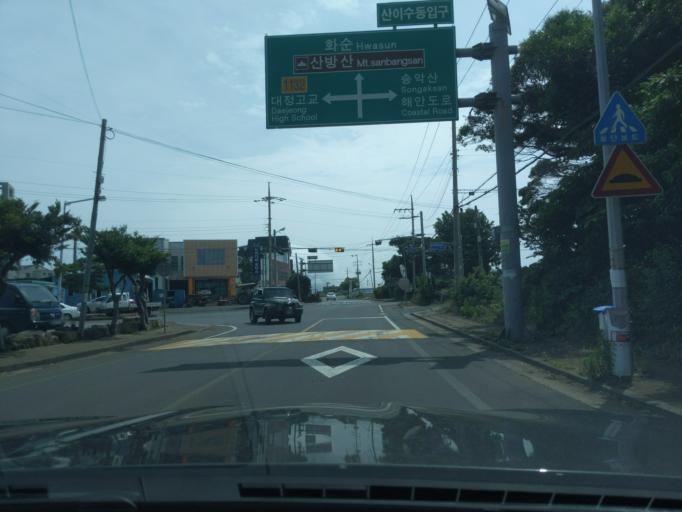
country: KR
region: Jeju-do
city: Gaigeturi
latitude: 33.2250
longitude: 126.2652
